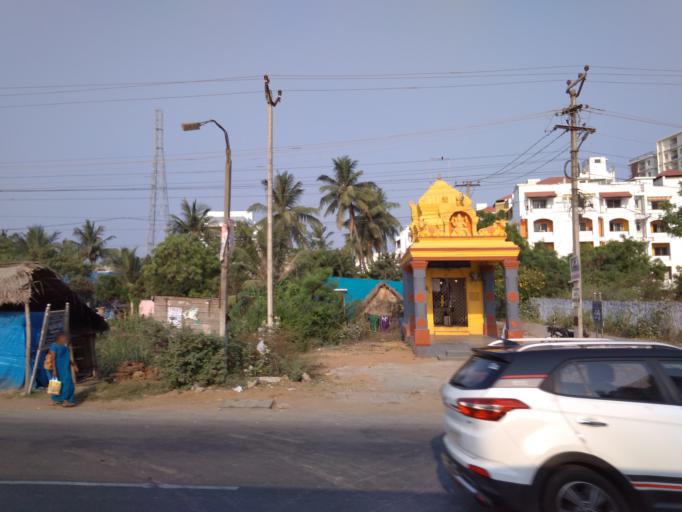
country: IN
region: Tamil Nadu
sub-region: Kancheepuram
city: Injambakkam
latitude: 12.8201
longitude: 80.2305
